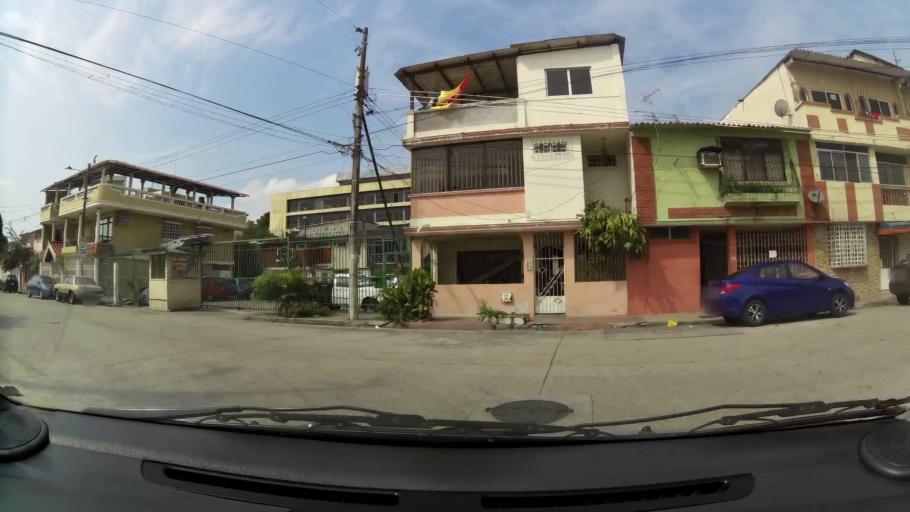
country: EC
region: Guayas
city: Guayaquil
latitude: -2.2427
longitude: -79.8972
